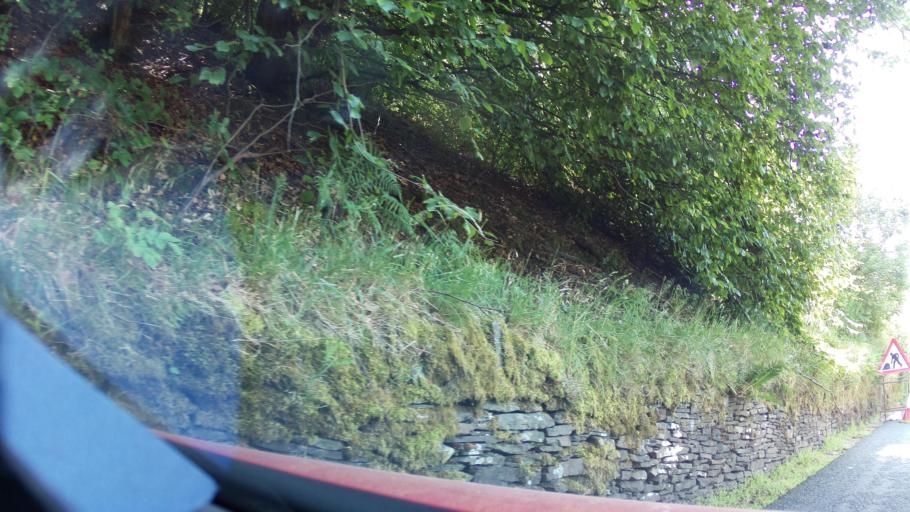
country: GB
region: Wales
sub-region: Caerphilly County Borough
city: New Tredegar
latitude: 51.7145
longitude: -3.2382
